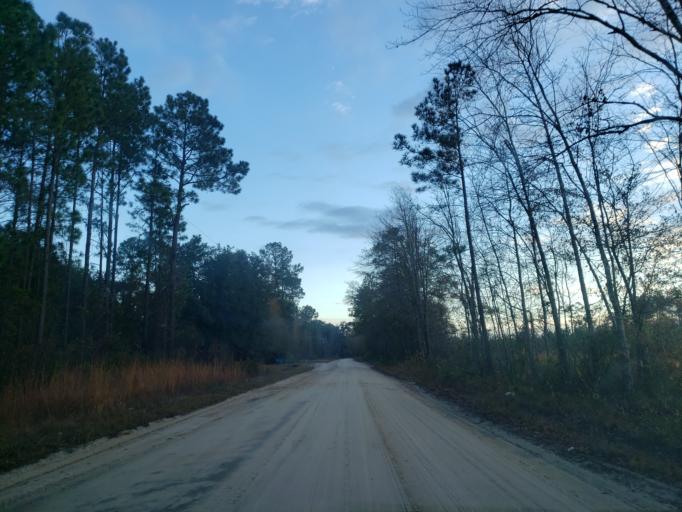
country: US
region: Georgia
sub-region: Chatham County
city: Bloomingdale
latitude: 32.1233
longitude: -81.3289
